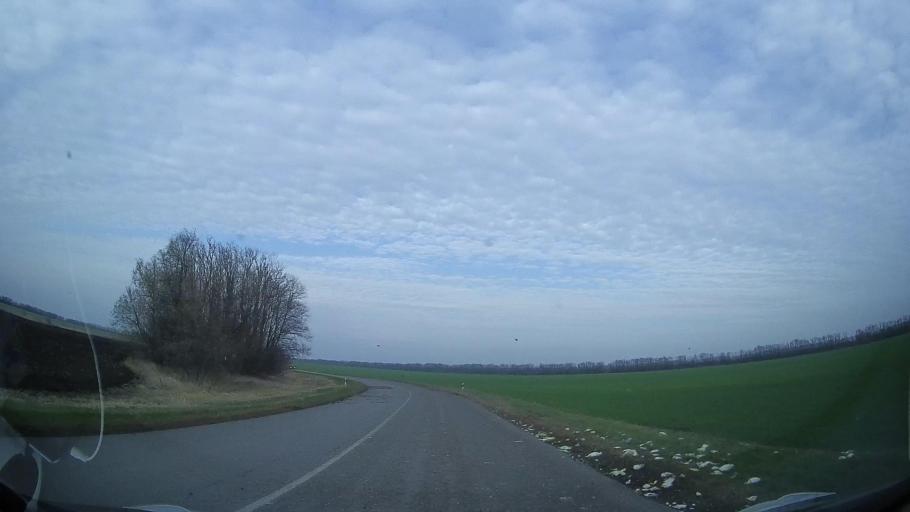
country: RU
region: Rostov
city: Zernograd
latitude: 46.9664
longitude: 40.3906
